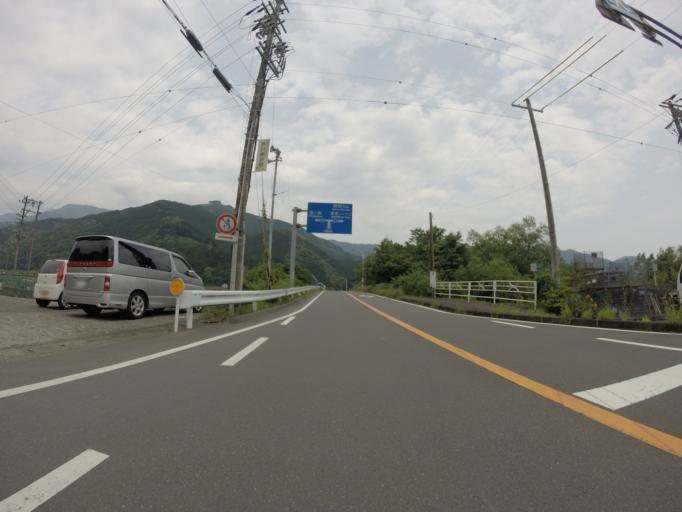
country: JP
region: Shizuoka
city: Shizuoka-shi
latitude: 35.1133
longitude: 138.3558
